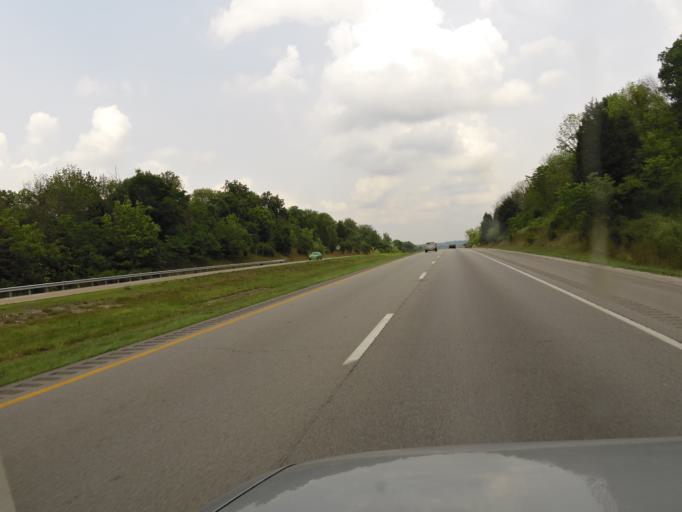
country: US
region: Indiana
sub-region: Switzerland County
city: Vevay
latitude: 38.6784
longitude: -84.9780
